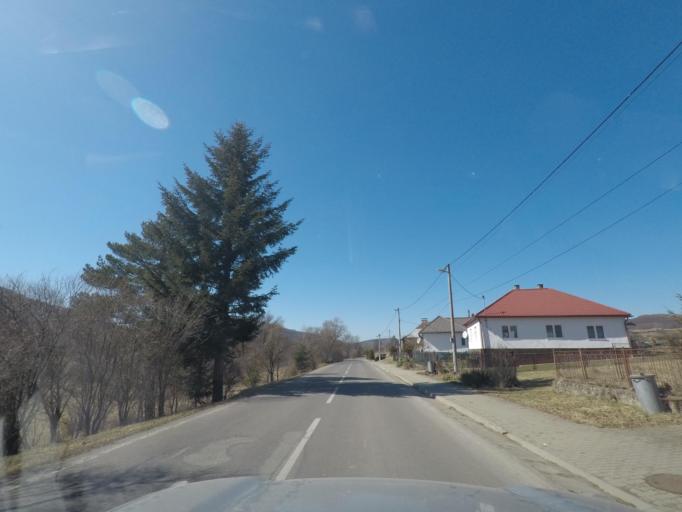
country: UA
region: Zakarpattia
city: Velykyi Bereznyi
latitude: 48.8943
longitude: 22.4053
